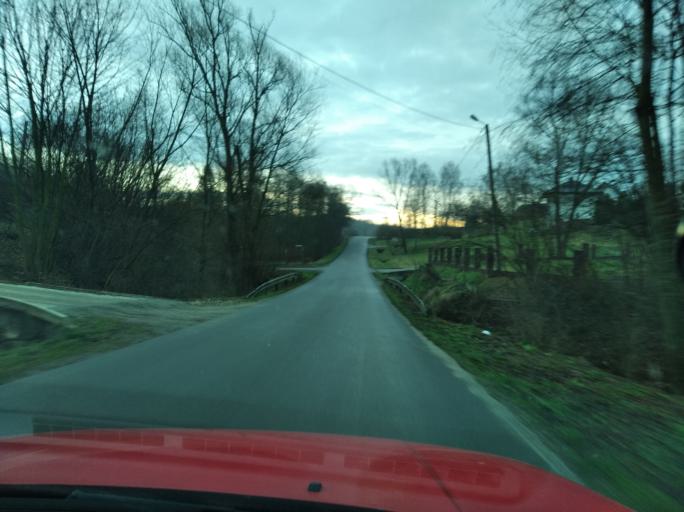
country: PL
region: Subcarpathian Voivodeship
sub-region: Powiat strzyzowski
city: Niebylec
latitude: 49.8713
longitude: 21.8787
